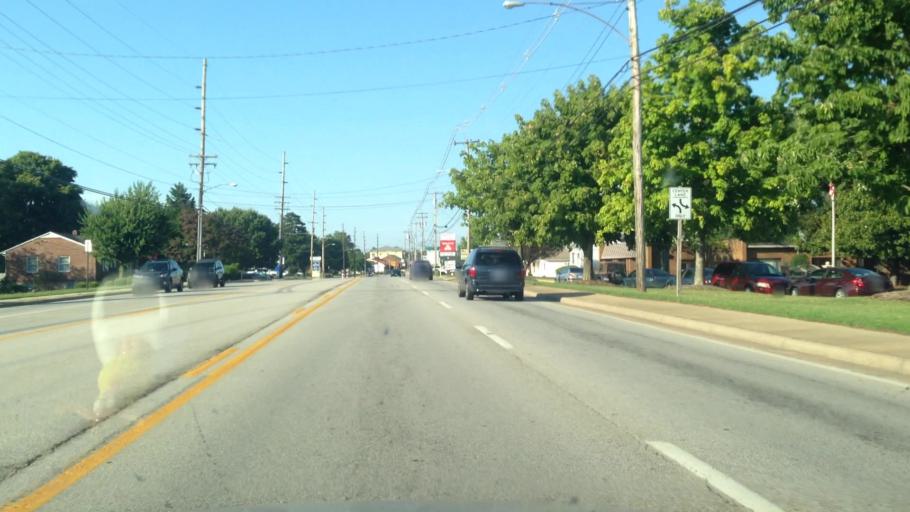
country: US
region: Virginia
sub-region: City of Danville
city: Danville
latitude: 36.6049
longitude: -79.4117
